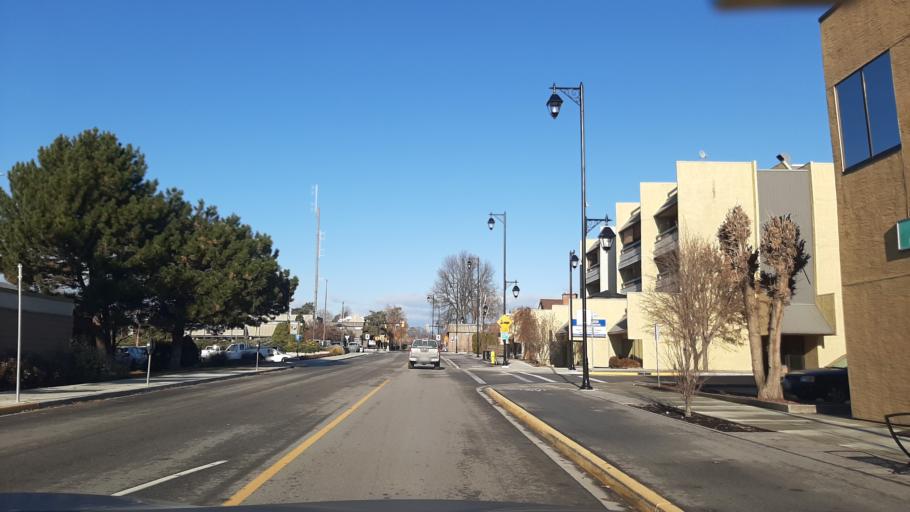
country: CA
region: British Columbia
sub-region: Regional District of North Okanagan
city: Vernon
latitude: 50.2657
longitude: -119.2707
